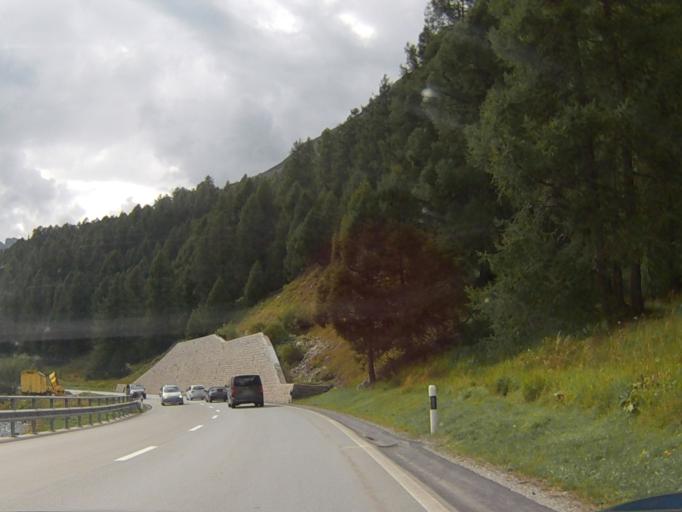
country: CH
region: Grisons
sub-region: Maloja District
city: Silvaplana
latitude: 46.4328
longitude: 9.7464
